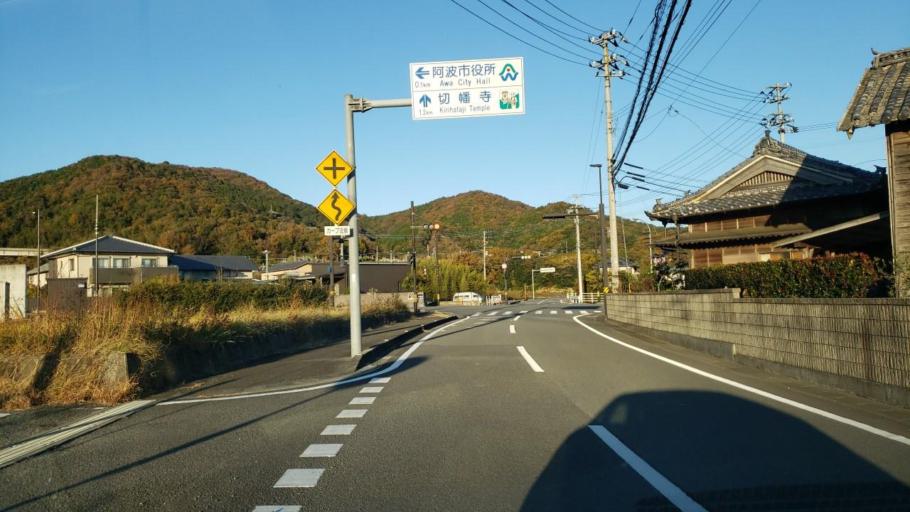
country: JP
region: Tokushima
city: Kamojimacho-jogejima
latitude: 34.1004
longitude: 134.2986
